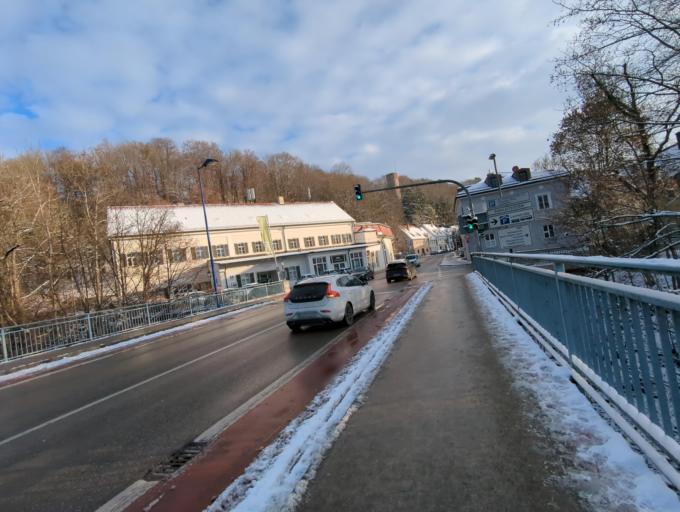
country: DE
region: Bavaria
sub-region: Upper Bavaria
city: Landsberg am Lech
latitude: 48.0546
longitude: 10.8764
